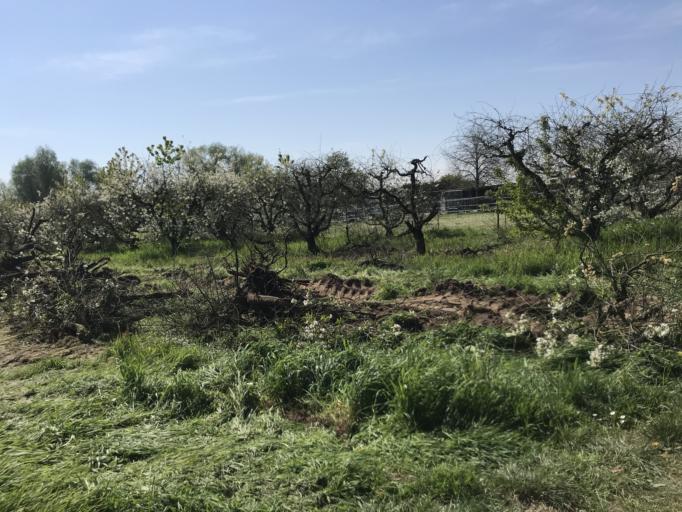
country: DE
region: Hesse
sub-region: Regierungsbezirk Darmstadt
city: Eltville
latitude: 50.0056
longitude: 8.0977
